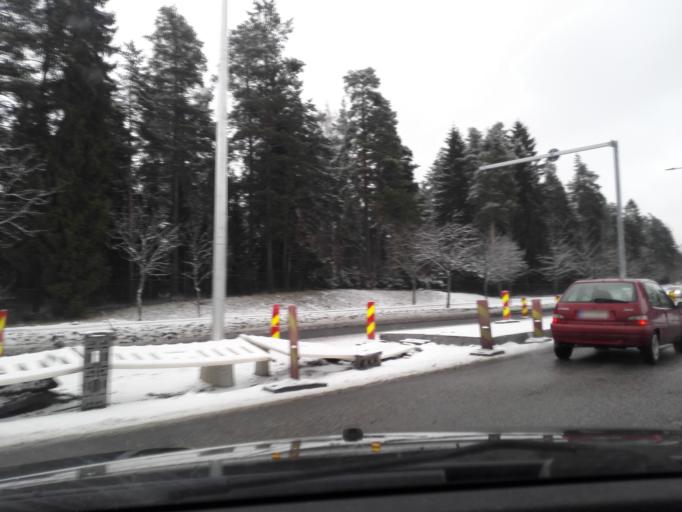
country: FI
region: Uusimaa
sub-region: Helsinki
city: Vantaa
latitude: 60.2890
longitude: 25.0764
